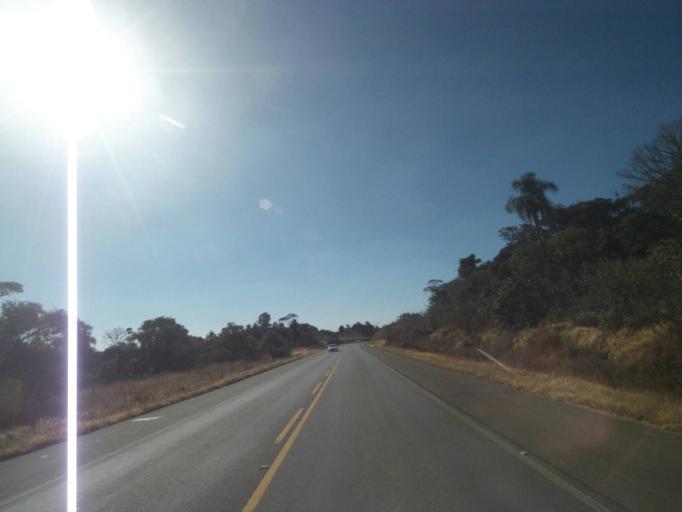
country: BR
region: Parana
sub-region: Tibagi
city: Tibagi
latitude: -24.7586
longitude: -50.4699
